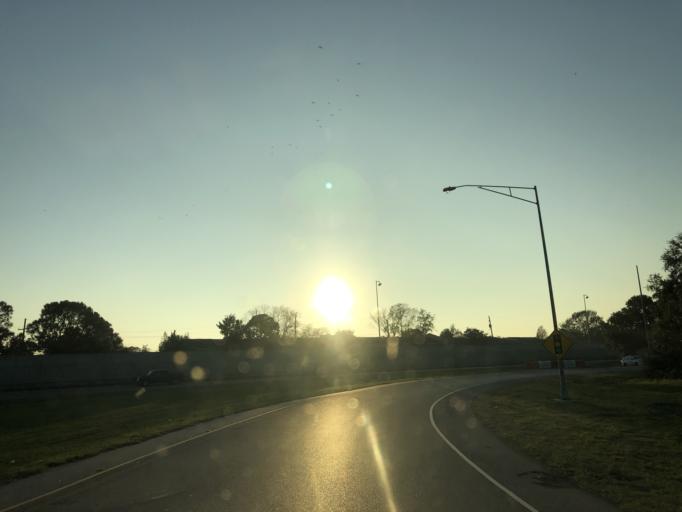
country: US
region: Louisiana
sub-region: Jefferson Parish
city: Kenner
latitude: 30.0041
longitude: -90.2091
